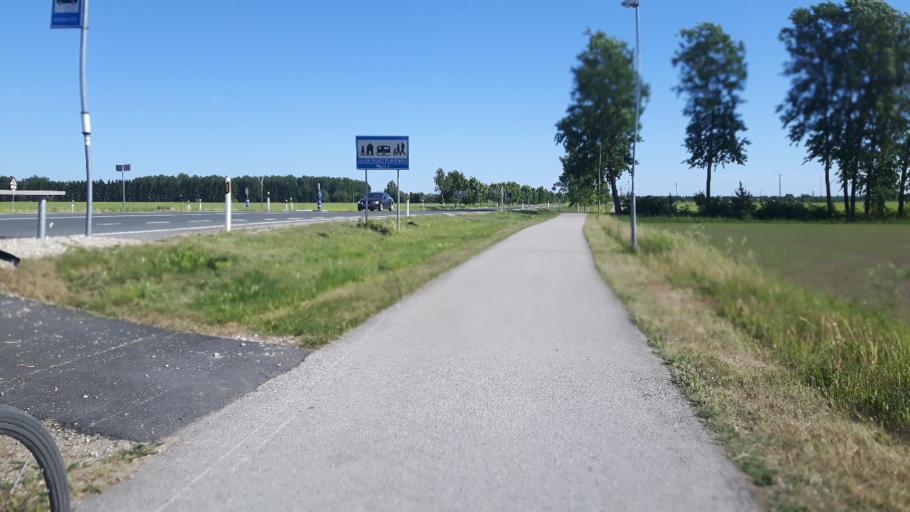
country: EE
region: Raplamaa
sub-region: Kehtna vald
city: Kehtna
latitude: 58.9409
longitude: 24.8793
